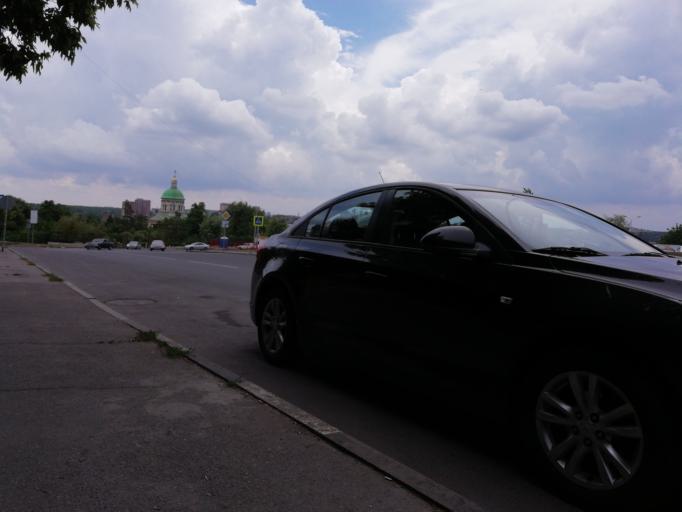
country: RU
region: Rostov
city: Severnyy
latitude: 47.2908
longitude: 39.7186
